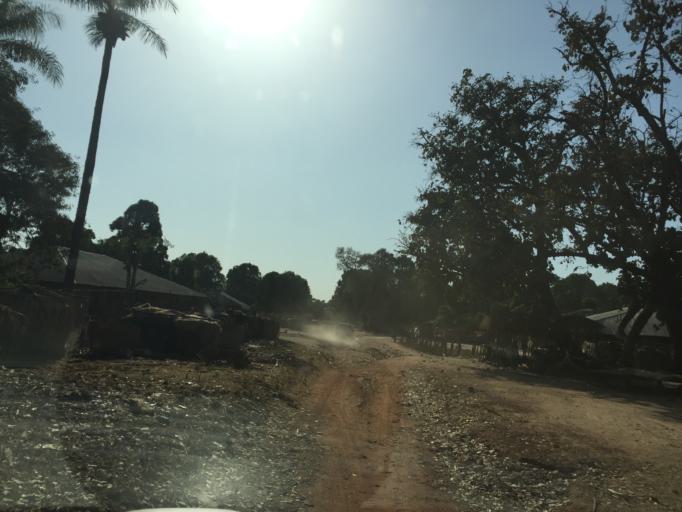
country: GW
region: Oio
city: Farim
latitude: 12.4606
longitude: -15.3023
